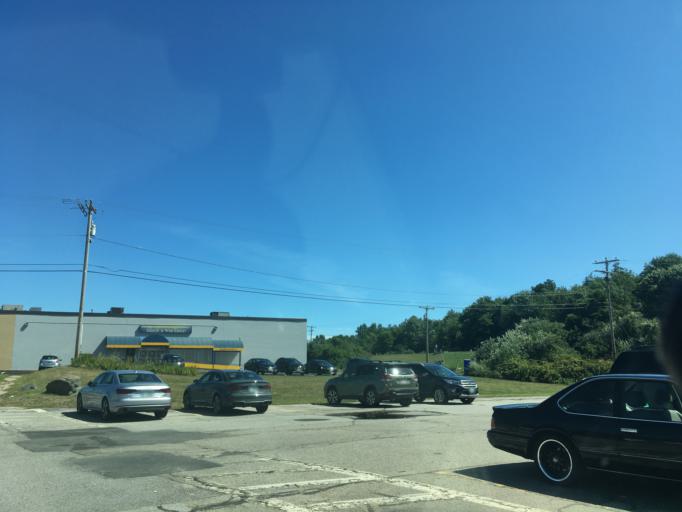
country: US
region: New Hampshire
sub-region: Rockingham County
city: Exeter
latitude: 42.9968
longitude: -70.9226
